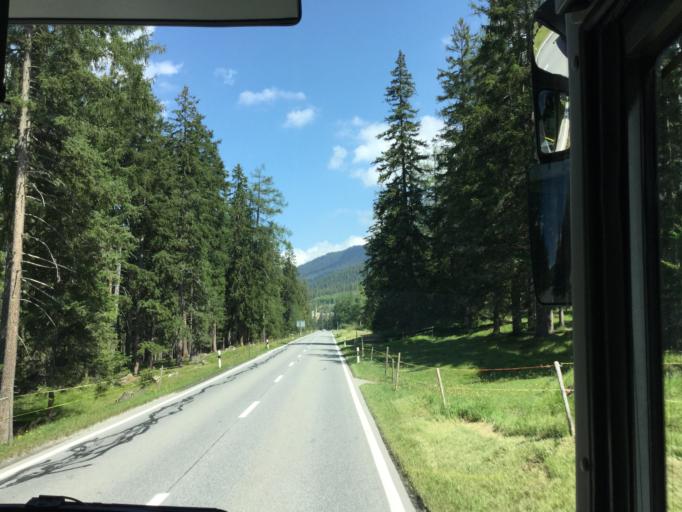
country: CH
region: Grisons
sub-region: Albula District
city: Tiefencastel
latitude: 46.7007
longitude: 9.5586
